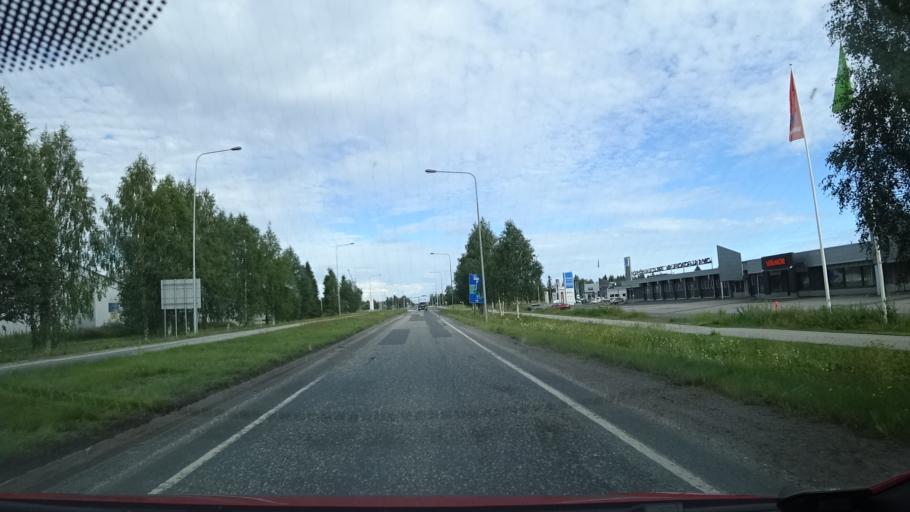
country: FI
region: Lapland
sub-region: Kemi-Tornio
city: Keminmaa
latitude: 65.7990
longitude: 24.5075
